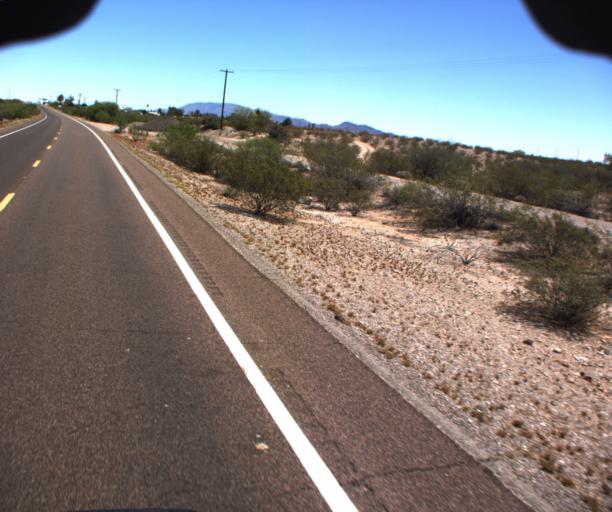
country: US
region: Arizona
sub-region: La Paz County
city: Salome
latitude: 33.7570
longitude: -113.6605
